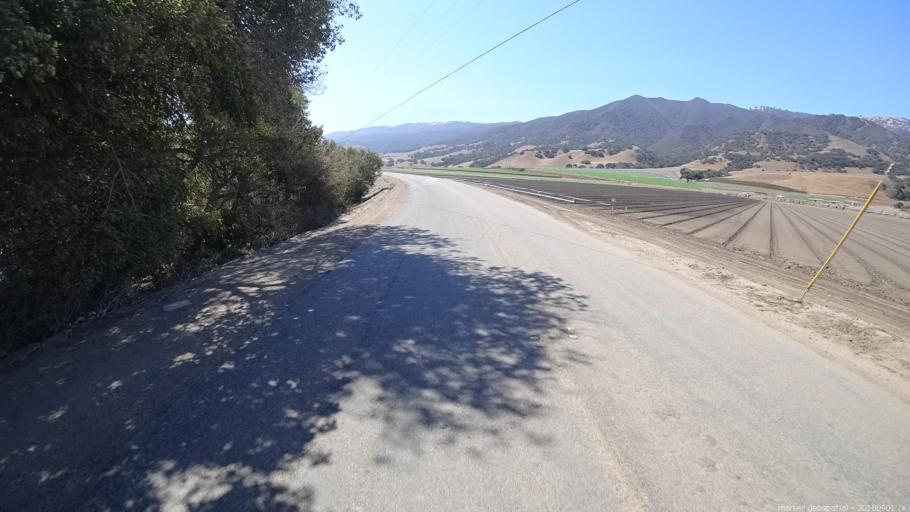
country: US
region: California
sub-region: Monterey County
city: Chualar
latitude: 36.5524
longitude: -121.5497
